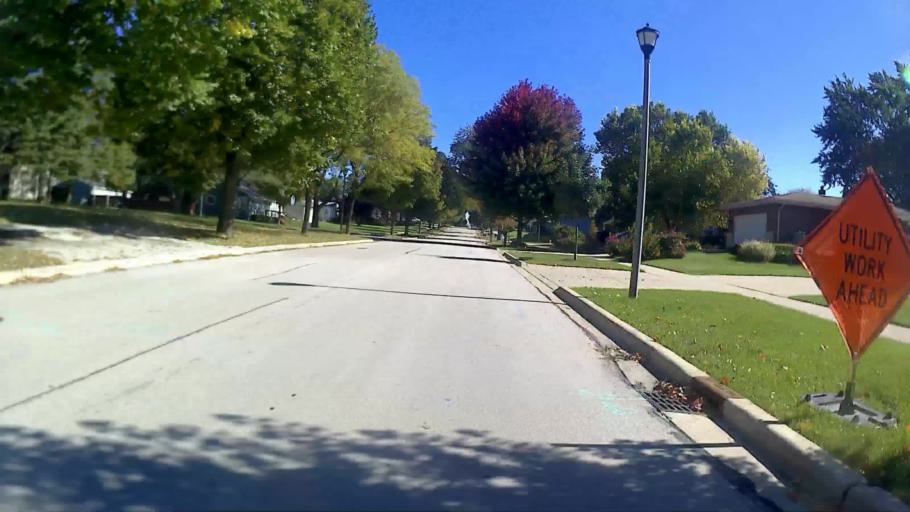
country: US
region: Illinois
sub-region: DuPage County
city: Lombard
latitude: 41.9007
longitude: -88.0117
